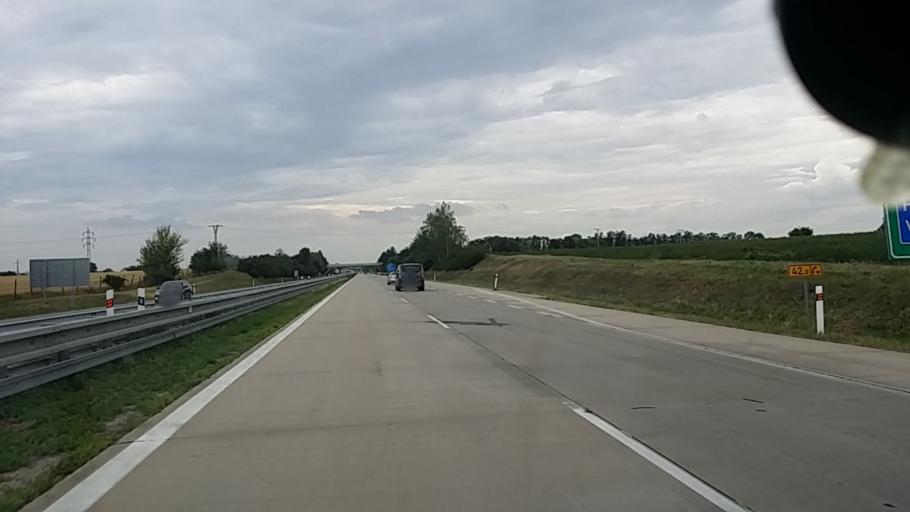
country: CZ
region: South Moravian
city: Podivin
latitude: 48.8286
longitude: 16.8730
